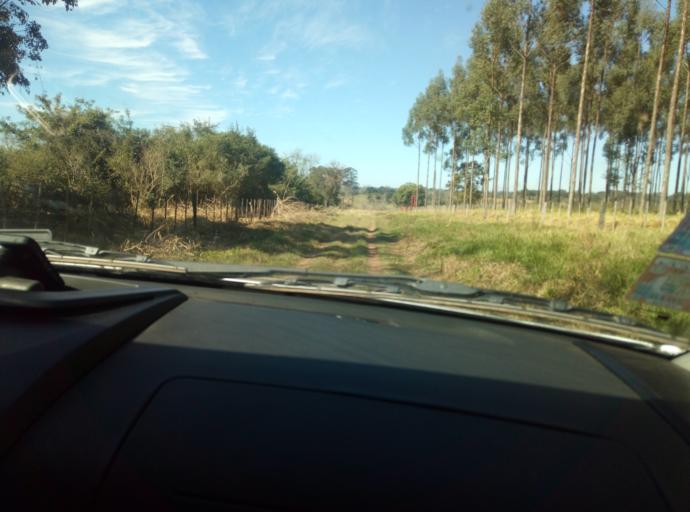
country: PY
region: Caaguazu
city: Carayao
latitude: -25.1765
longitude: -56.3019
